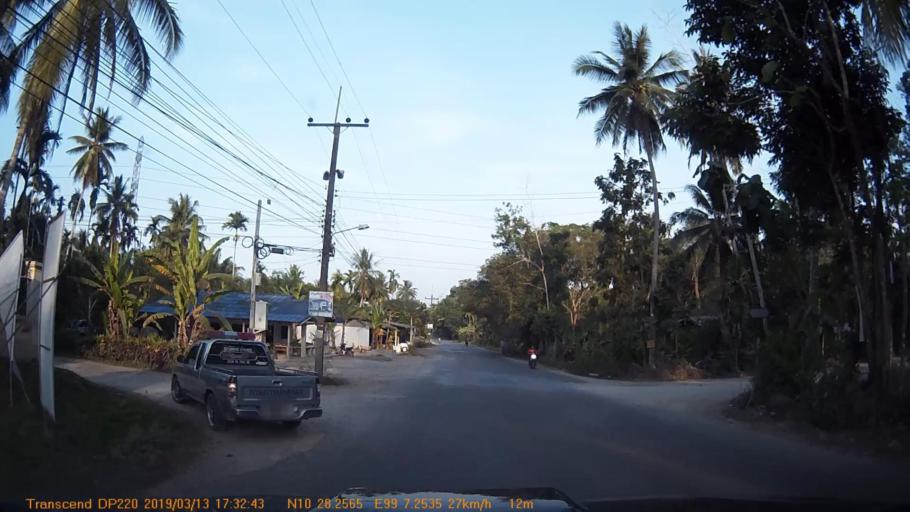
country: TH
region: Chumphon
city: Chumphon
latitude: 10.4710
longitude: 99.1212
